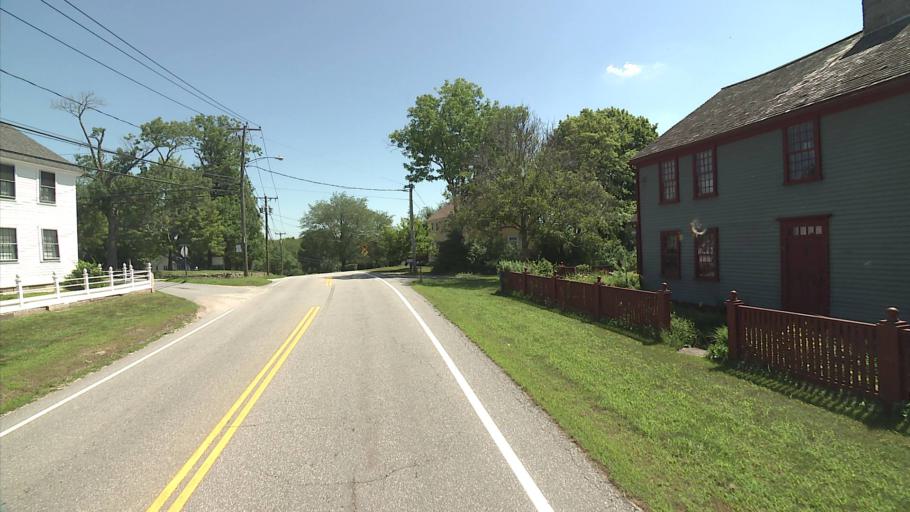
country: US
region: Connecticut
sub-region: Windham County
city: Moosup
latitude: 41.6903
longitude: -71.8468
